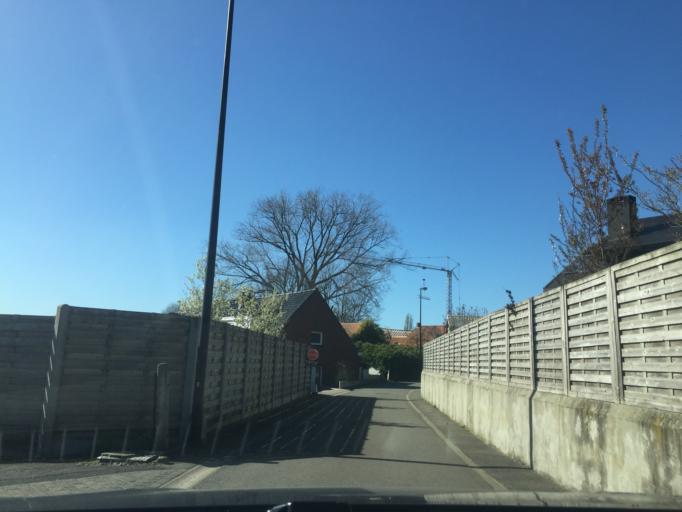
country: BE
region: Flanders
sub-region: Provincie West-Vlaanderen
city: Hooglede
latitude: 50.9792
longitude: 3.0720
